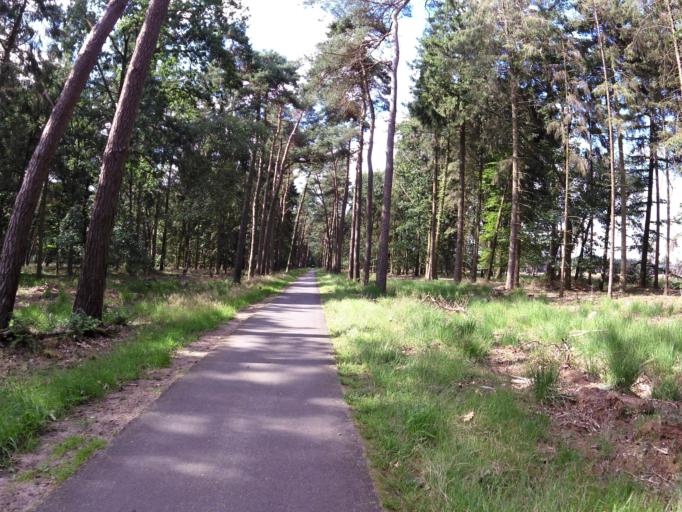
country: NL
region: North Brabant
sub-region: Gemeente Valkenswaard
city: Valkenswaard
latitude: 51.3544
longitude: 5.5138
